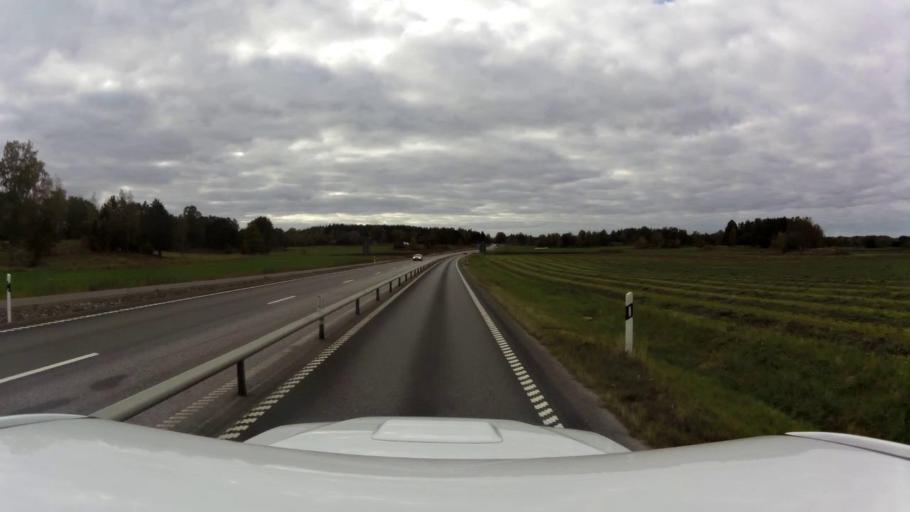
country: SE
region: OEstergoetland
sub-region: Linkopings Kommun
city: Malmslatt
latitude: 58.3102
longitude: 15.5668
